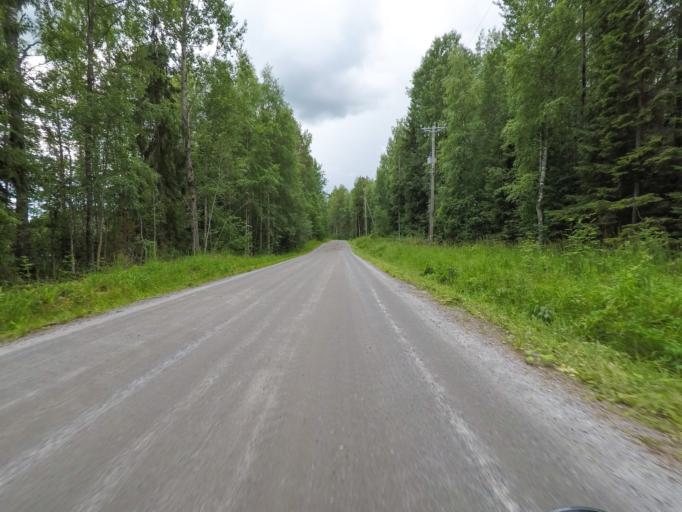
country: FI
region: Central Finland
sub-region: Jyvaeskylae
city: Hankasalmi
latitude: 62.4284
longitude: 26.6450
